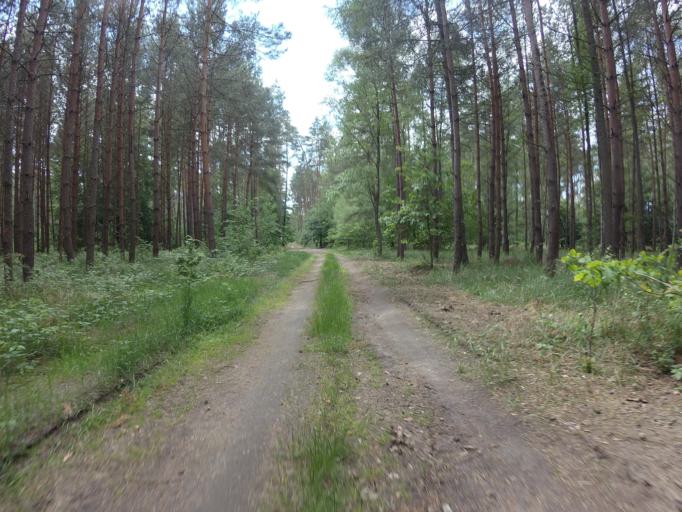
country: PL
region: West Pomeranian Voivodeship
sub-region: Powiat choszczenski
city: Krzecin
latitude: 53.0174
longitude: 15.5507
